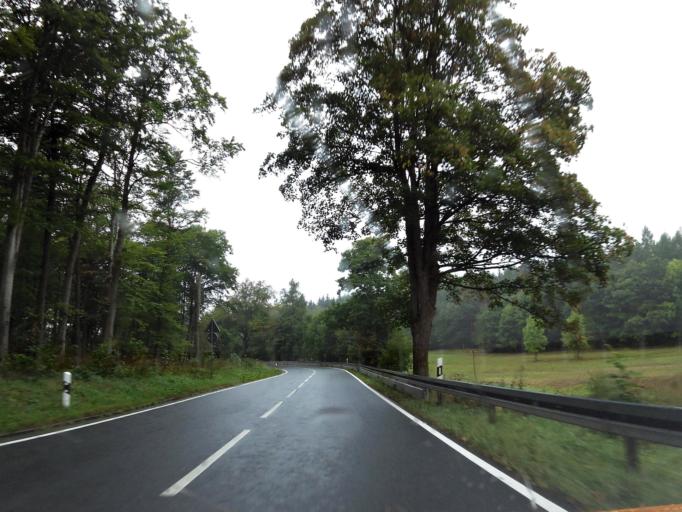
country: DE
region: Saxony-Anhalt
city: Hasselfelde
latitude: 51.6626
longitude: 10.9048
